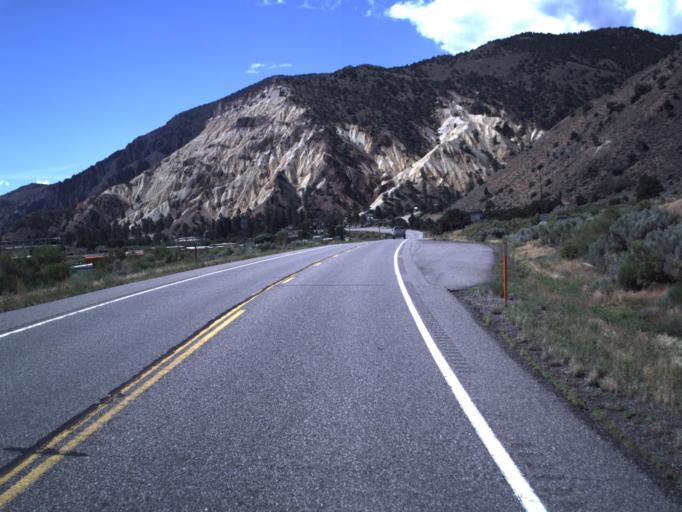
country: US
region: Utah
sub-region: Sevier County
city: Monroe
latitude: 38.5228
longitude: -112.2655
